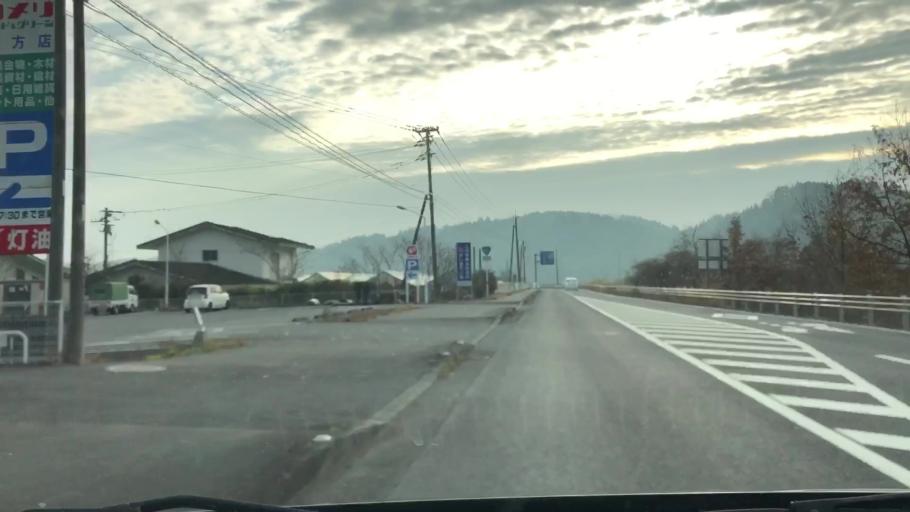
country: JP
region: Oita
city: Takedamachi
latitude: 32.9660
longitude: 131.4816
